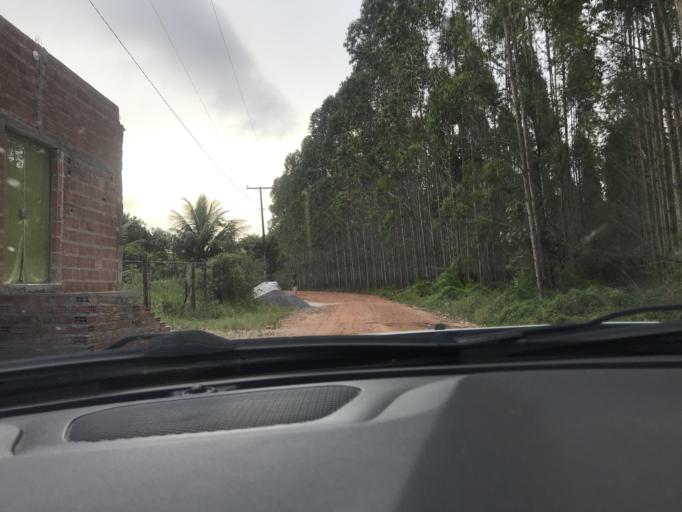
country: BR
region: Bahia
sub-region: Entre Rios
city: Entre Rios
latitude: -12.0955
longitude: -38.1926
